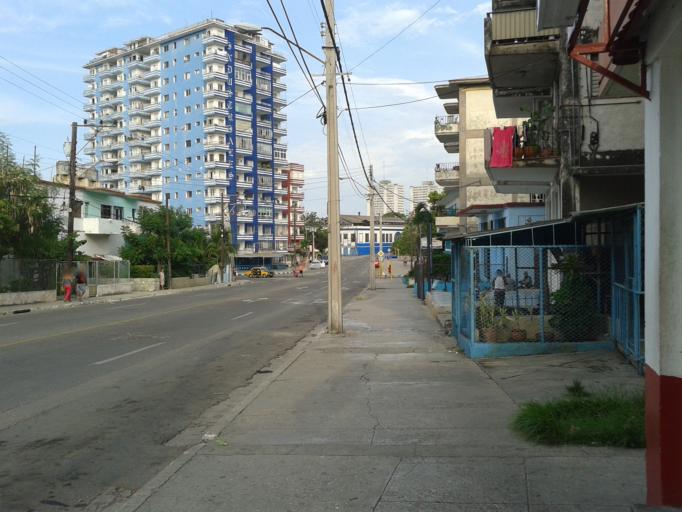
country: CU
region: La Habana
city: Cerro
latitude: 23.1203
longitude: -82.3776
